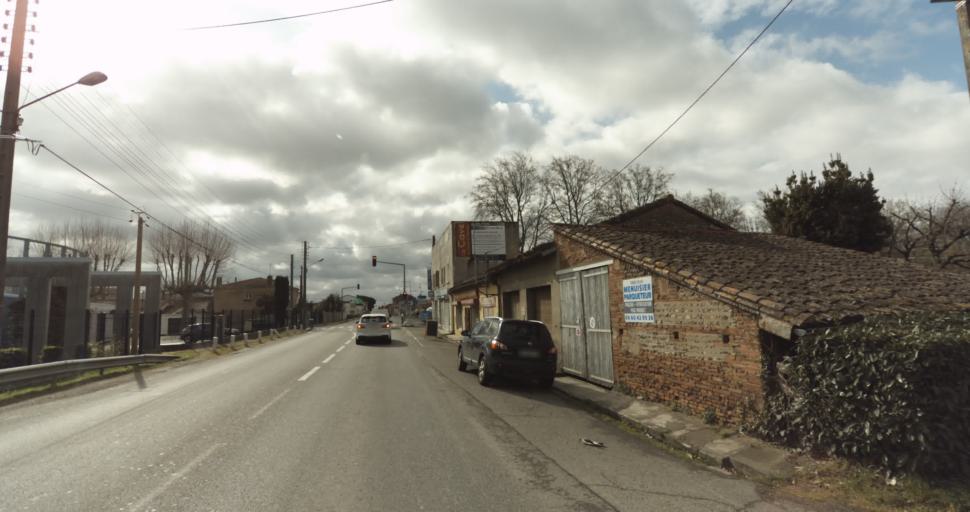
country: FR
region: Midi-Pyrenees
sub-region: Departement de la Haute-Garonne
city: Auterive
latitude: 43.3521
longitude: 1.4698
